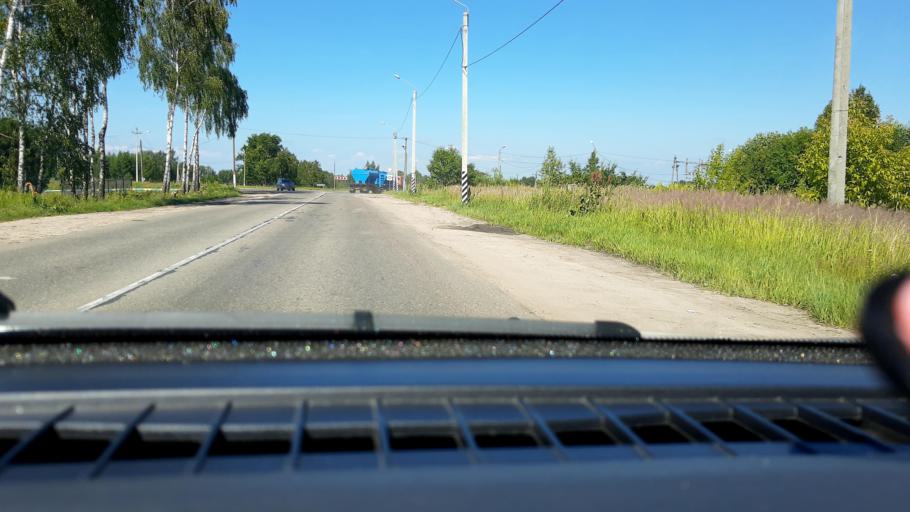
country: RU
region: Nizjnij Novgorod
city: Burevestnik
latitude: 56.1735
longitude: 43.7608
